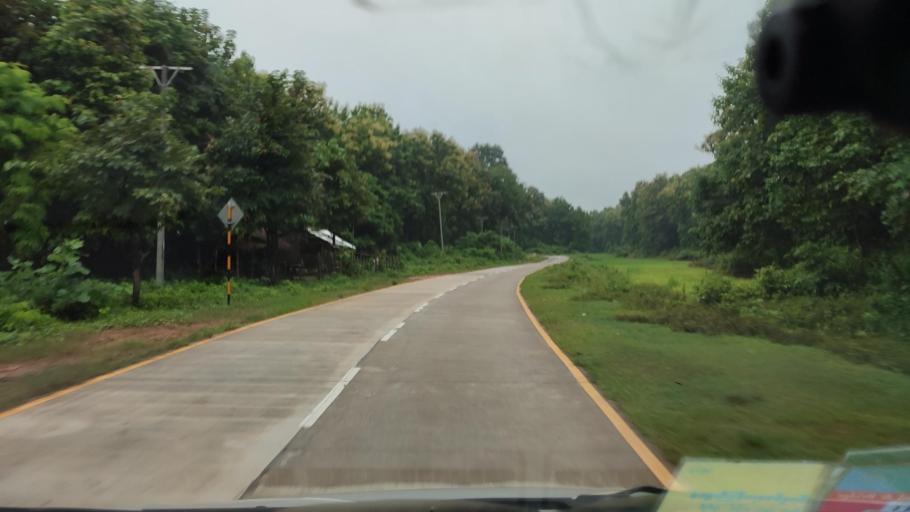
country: MM
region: Bago
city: Taungoo
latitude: 18.9867
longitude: 96.5164
